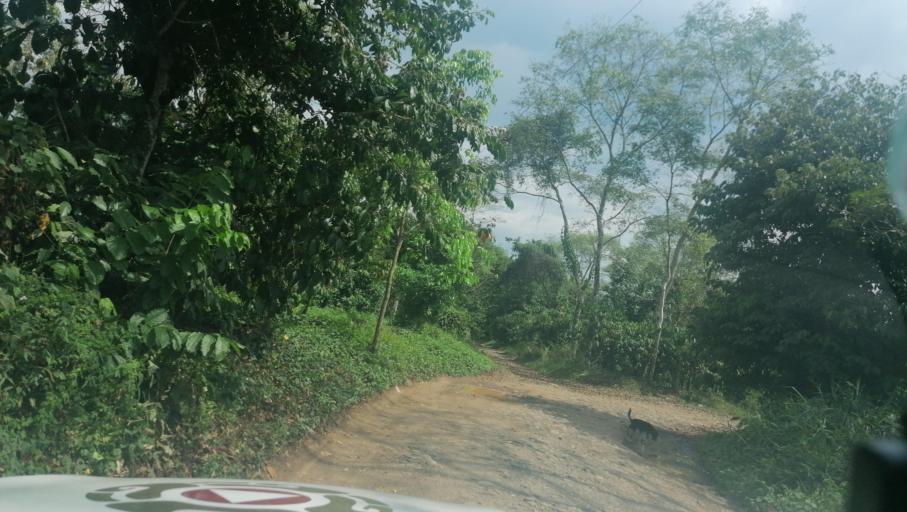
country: MX
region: Chiapas
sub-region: Cacahoatan
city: Benito Juarez
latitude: 15.0344
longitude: -92.2348
